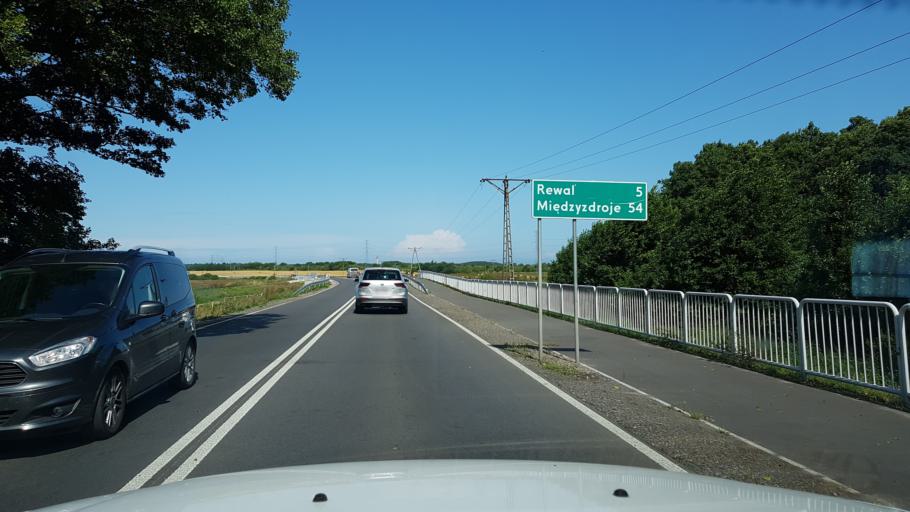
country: PL
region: West Pomeranian Voivodeship
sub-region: Powiat gryficki
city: Karnice
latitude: 54.0738
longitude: 15.0760
